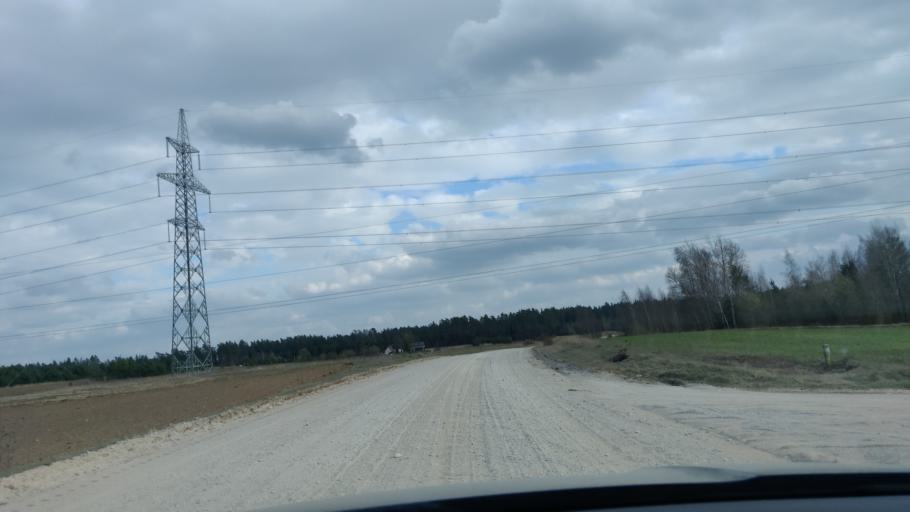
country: LT
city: Lentvaris
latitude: 54.6081
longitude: 25.0736
